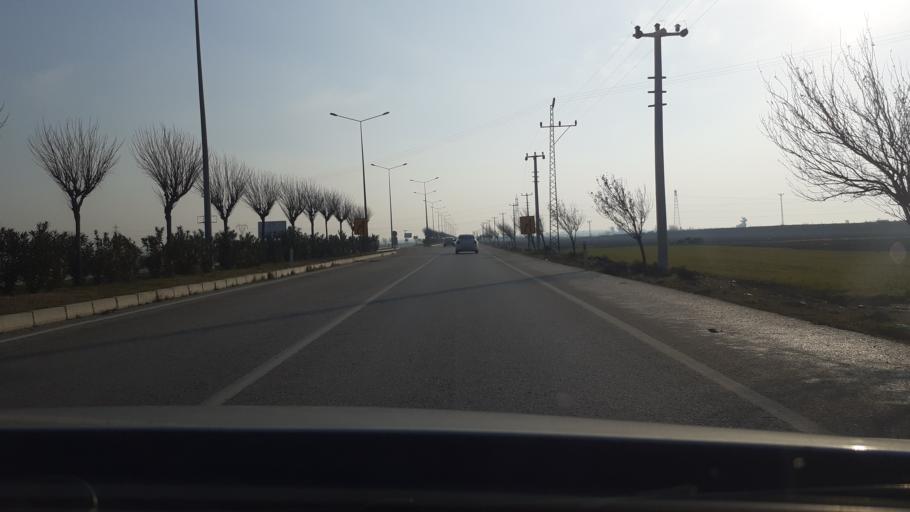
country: TR
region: Hatay
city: Serinyol
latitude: 36.3715
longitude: 36.2396
